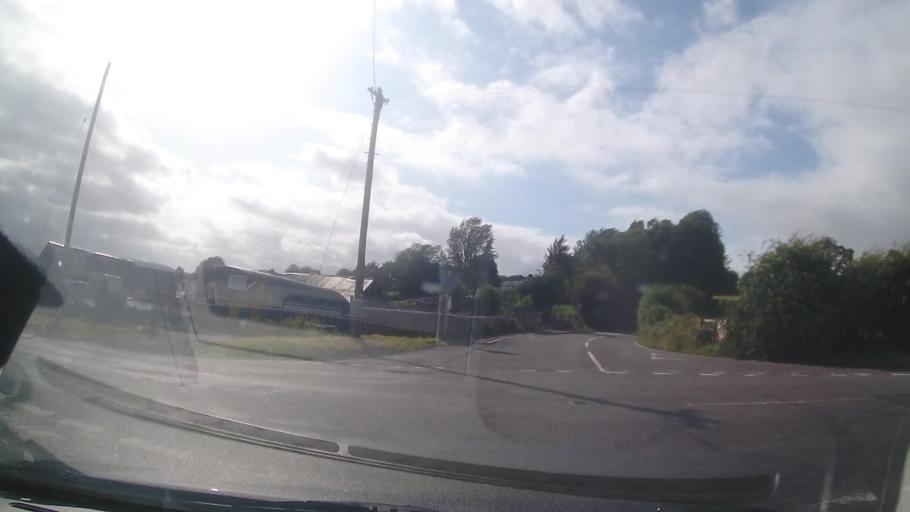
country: GB
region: England
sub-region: Shropshire
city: Bishop's Castle
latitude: 52.4962
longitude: -2.9880
